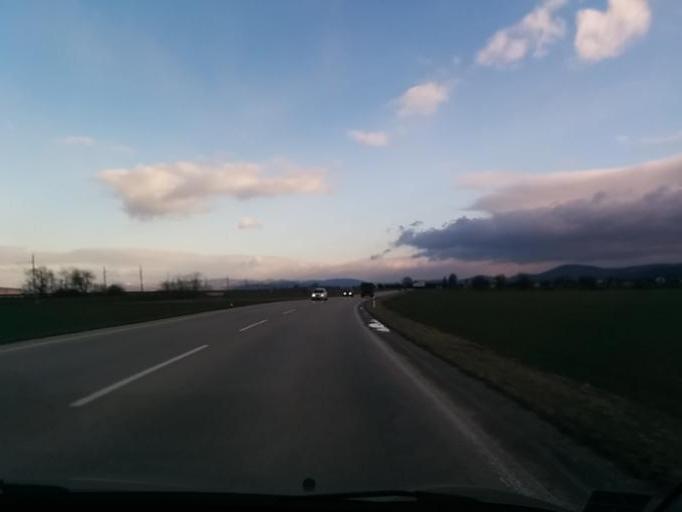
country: SK
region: Trnavsky
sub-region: Okres Trnava
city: Piestany
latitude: 48.6652
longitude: 17.8423
